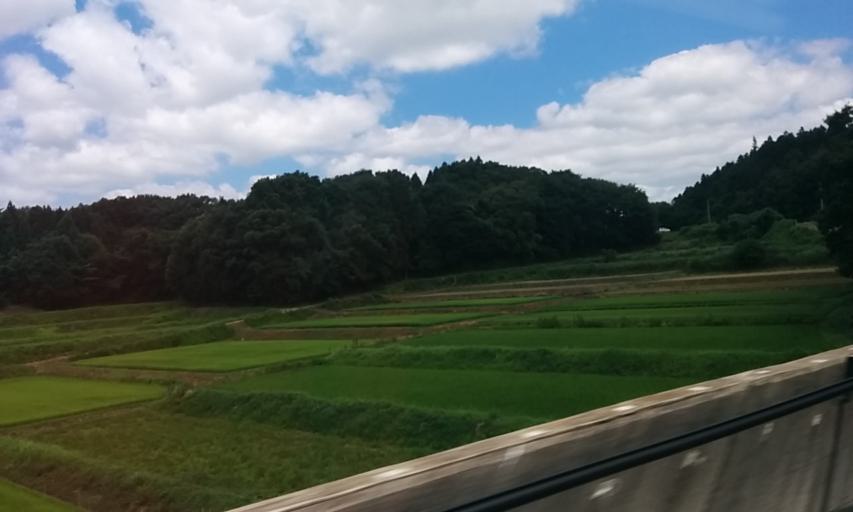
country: JP
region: Fukushima
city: Motomiya
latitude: 37.5284
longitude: 140.4387
